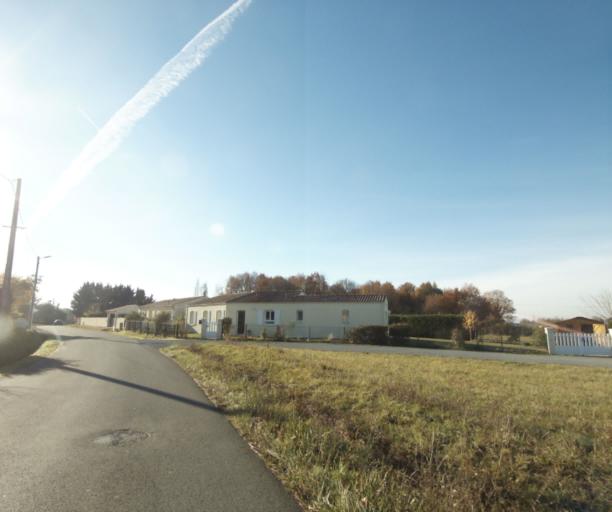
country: FR
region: Poitou-Charentes
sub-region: Departement de la Charente-Maritime
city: Fontcouverte
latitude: 45.7467
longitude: -0.5736
